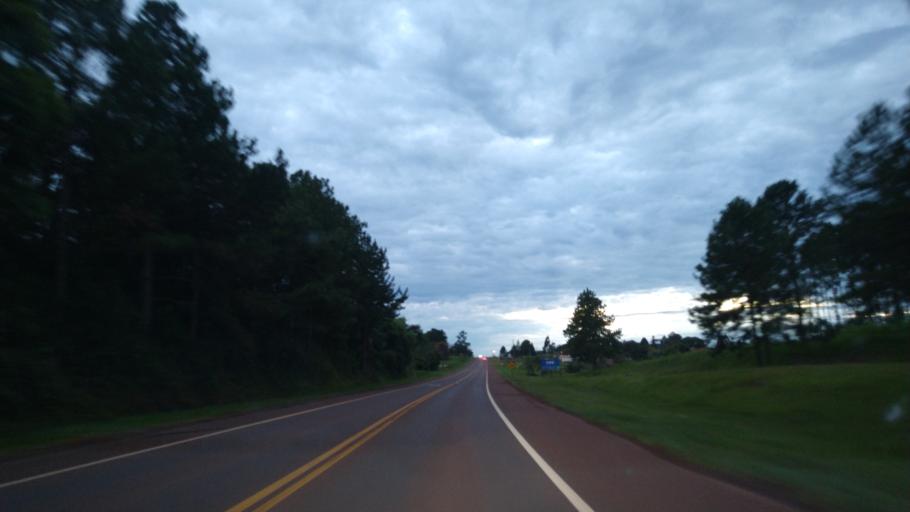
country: AR
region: Misiones
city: Dos de Mayo
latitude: -27.0064
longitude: -54.5119
